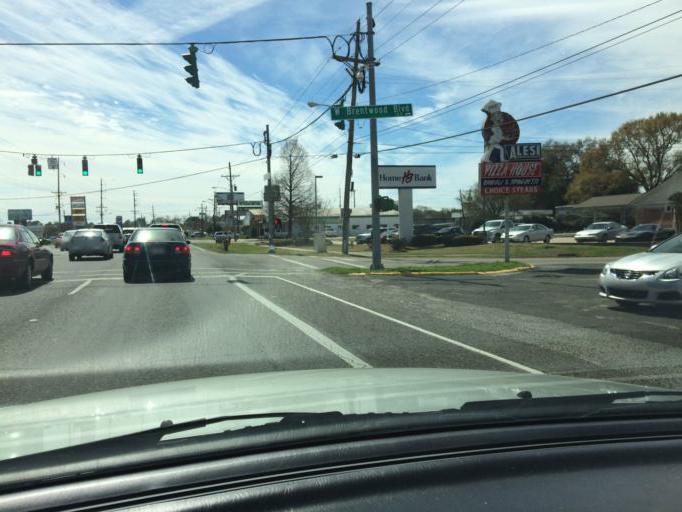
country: US
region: Louisiana
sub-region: Lafayette Parish
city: Lafayette
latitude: 30.1967
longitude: -92.0569
